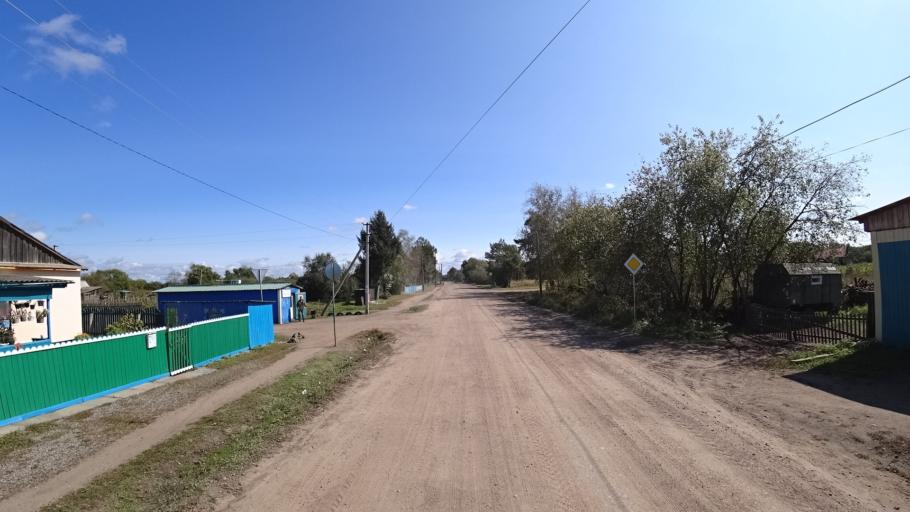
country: RU
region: Amur
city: Arkhara
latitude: 49.4024
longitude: 130.1437
